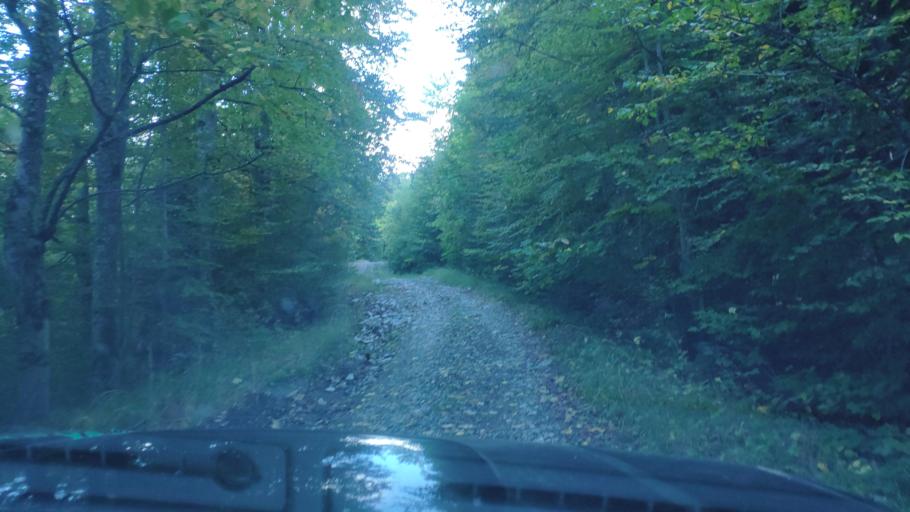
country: AL
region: Korce
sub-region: Rrethi i Devollit
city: Miras
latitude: 40.3614
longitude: 20.8958
